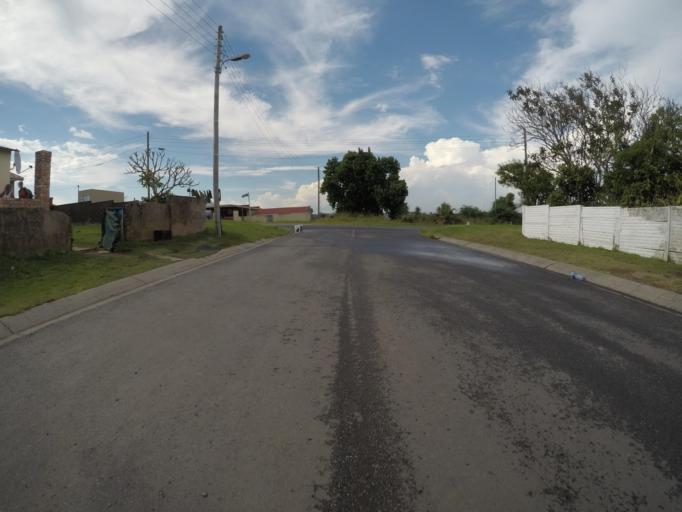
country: ZA
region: Eastern Cape
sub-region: Buffalo City Metropolitan Municipality
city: East London
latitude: -33.0231
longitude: 27.8770
